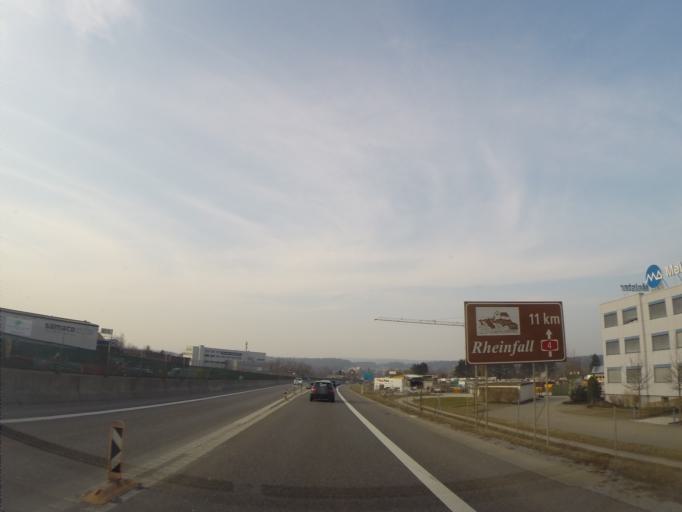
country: CH
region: Zurich
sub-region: Bezirk Andelfingen
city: Kleinandelfingen
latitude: 47.5925
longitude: 8.6902
